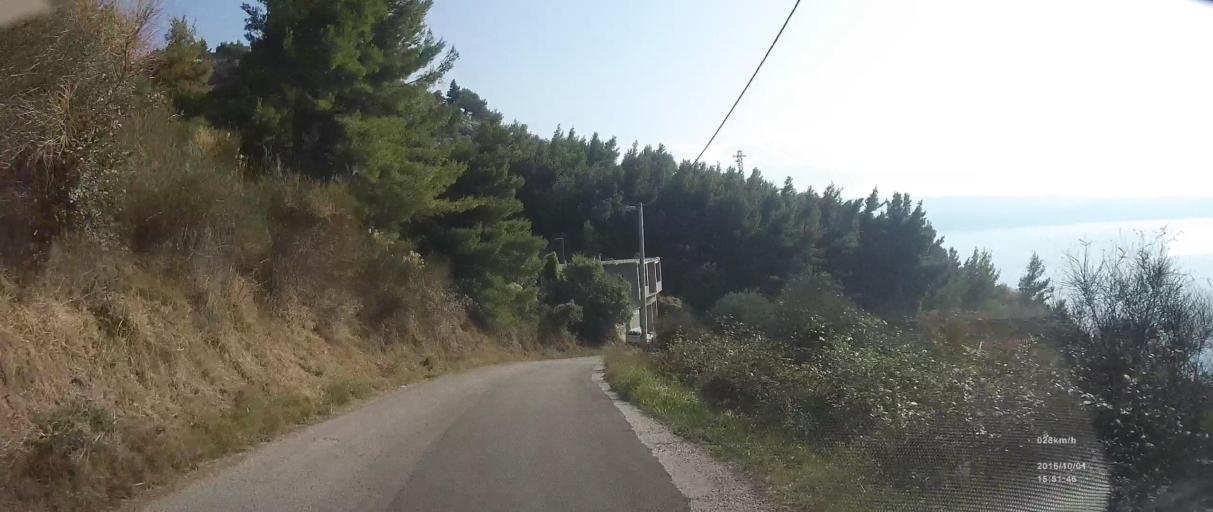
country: HR
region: Splitsko-Dalmatinska
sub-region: Grad Omis
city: Omis
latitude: 43.4372
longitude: 16.7060
